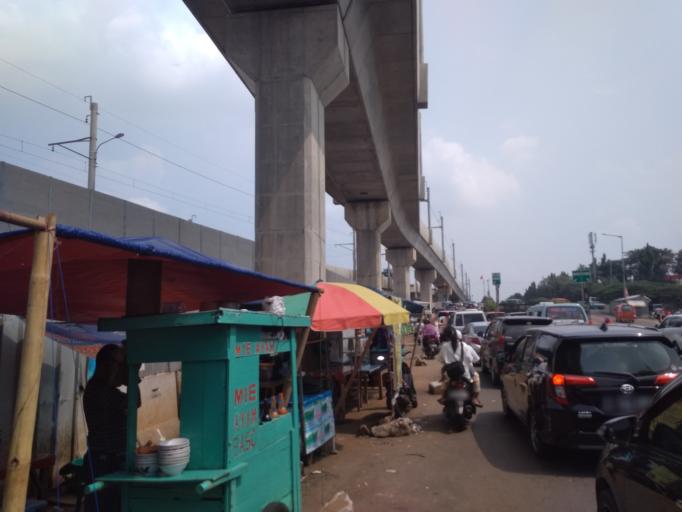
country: ID
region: Banten
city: South Tangerang
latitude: -6.2892
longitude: 106.7721
